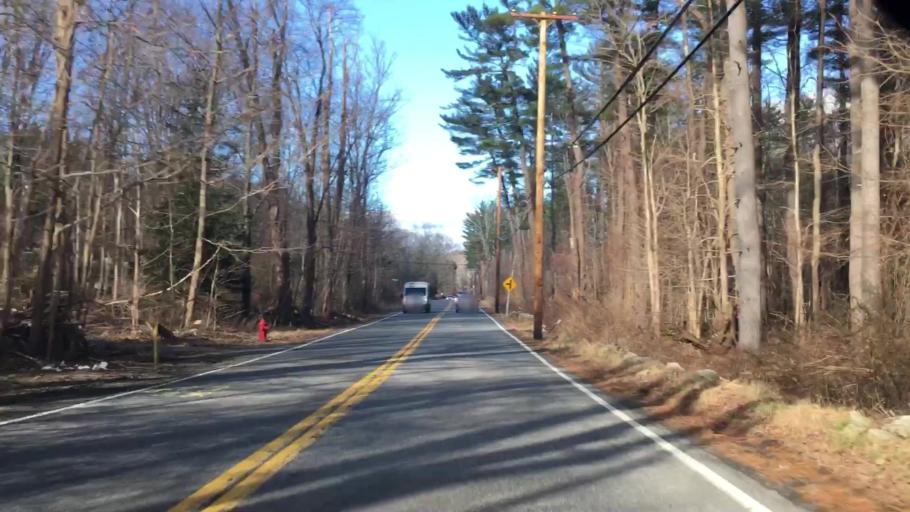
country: US
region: New York
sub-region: Putnam County
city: Carmel Hamlet
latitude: 41.4024
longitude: -73.6630
